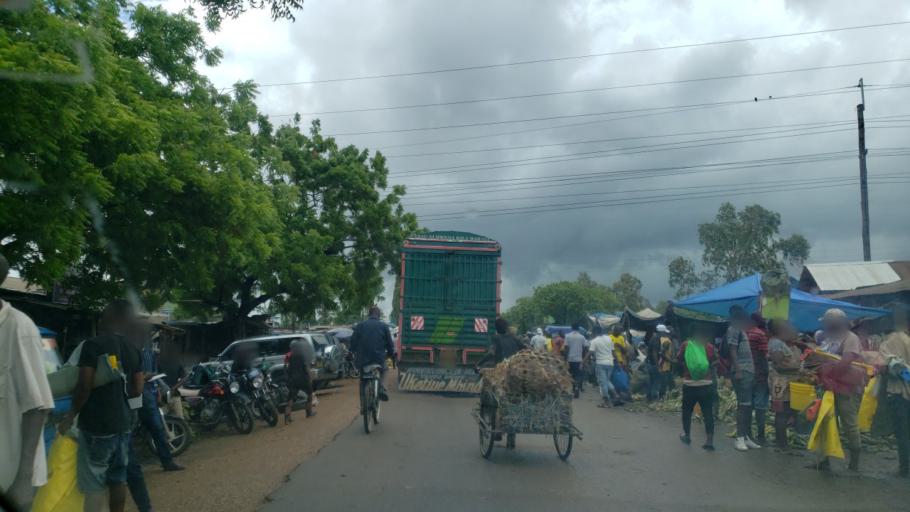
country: TZ
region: Dar es Salaam
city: Magomeni
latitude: -6.8016
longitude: 39.2249
